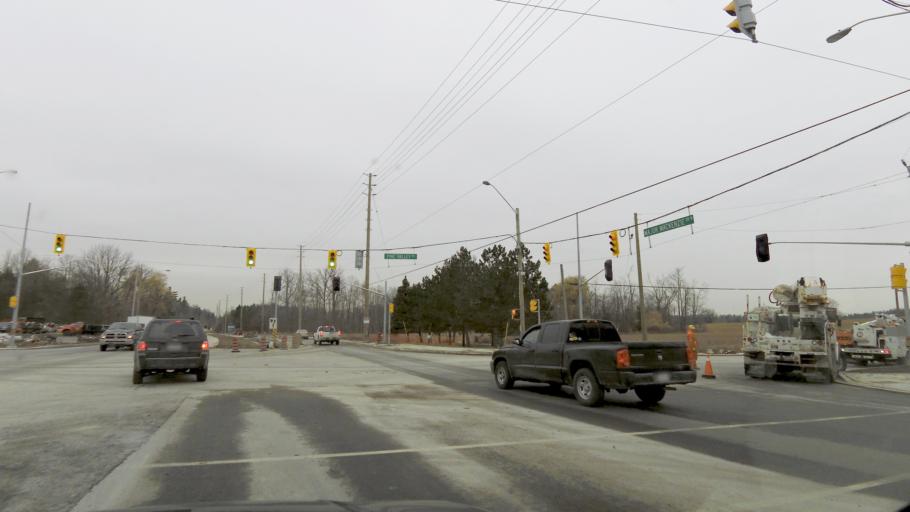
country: CA
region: Ontario
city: Vaughan
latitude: 43.8398
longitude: -79.5861
